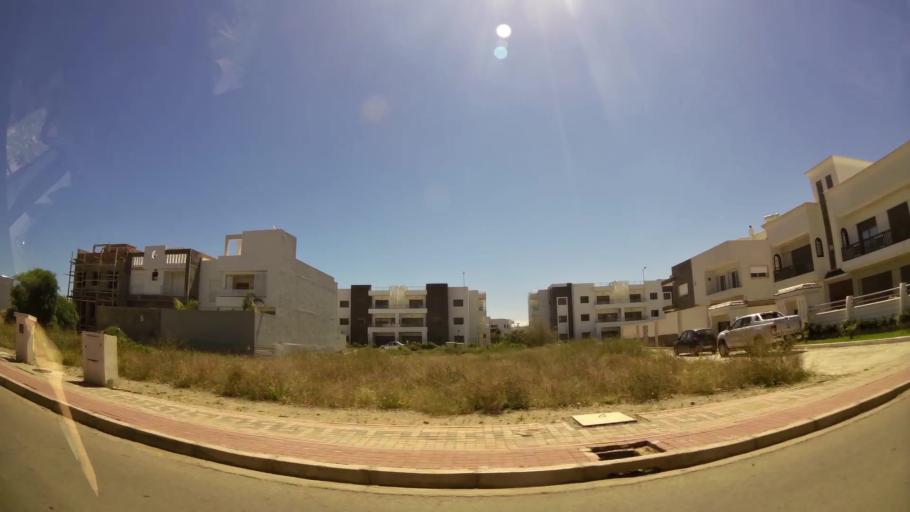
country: MA
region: Oriental
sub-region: Berkane-Taourirt
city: Madagh
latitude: 35.0939
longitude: -2.2654
